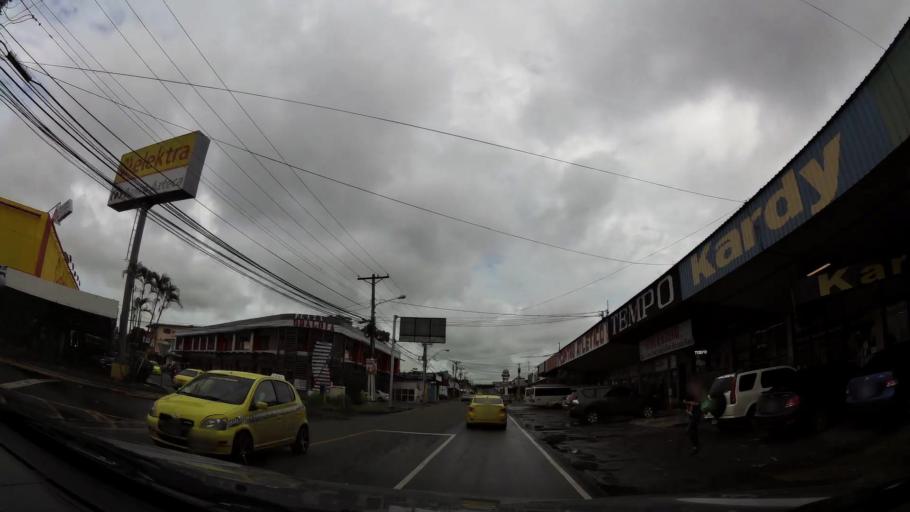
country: PA
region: Chiriqui
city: David
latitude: 8.4334
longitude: -82.4241
